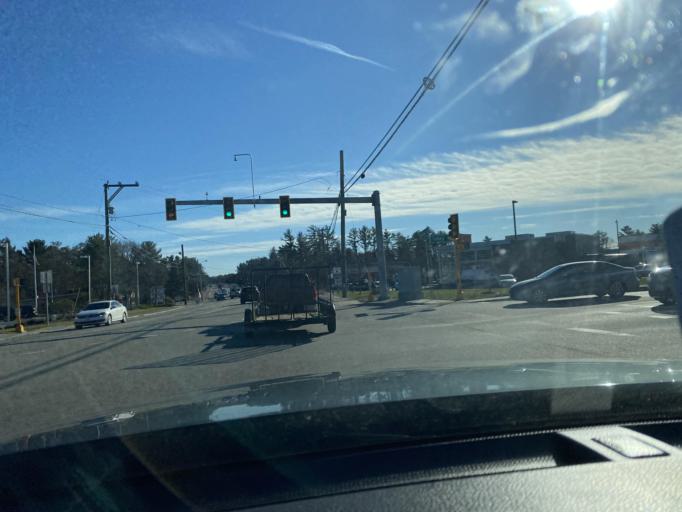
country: US
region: Massachusetts
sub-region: Plymouth County
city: West Wareham
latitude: 41.7812
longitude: -70.7440
